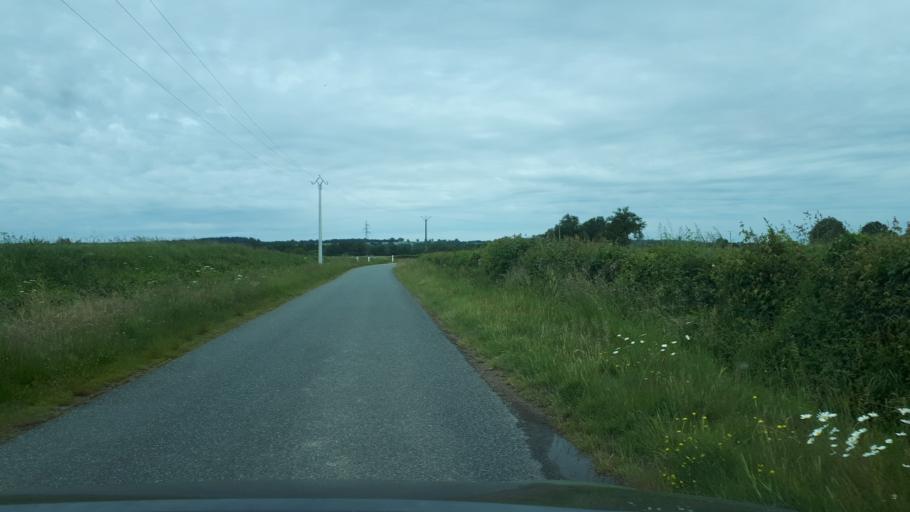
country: FR
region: Centre
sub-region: Departement du Cher
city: Henrichemont
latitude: 47.4046
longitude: 2.6431
